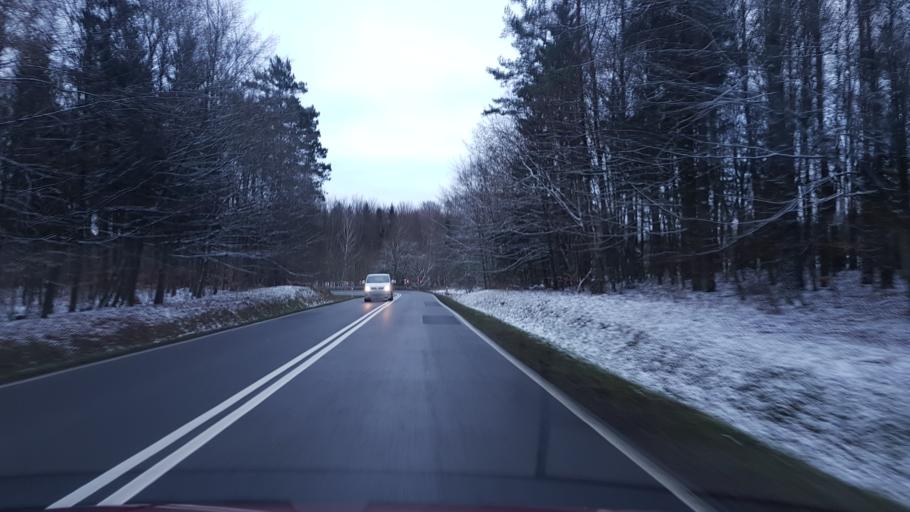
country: PL
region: Pomeranian Voivodeship
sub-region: Powiat bytowski
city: Miastko
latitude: 54.0120
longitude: 17.0585
